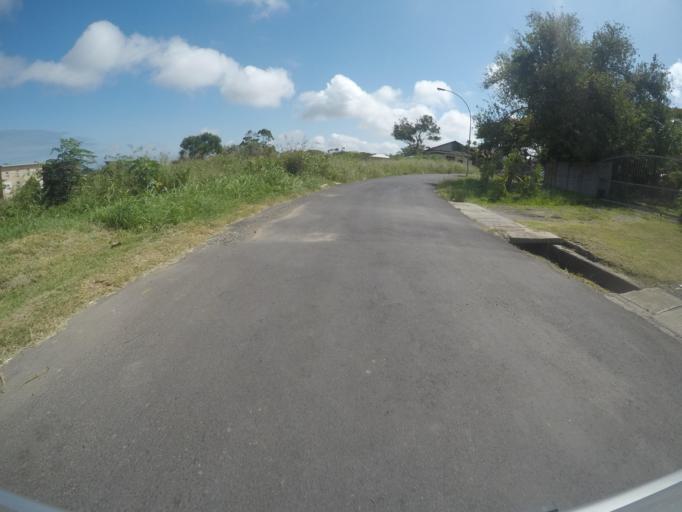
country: ZA
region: Eastern Cape
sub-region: Buffalo City Metropolitan Municipality
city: East London
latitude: -32.9975
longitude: 27.8942
